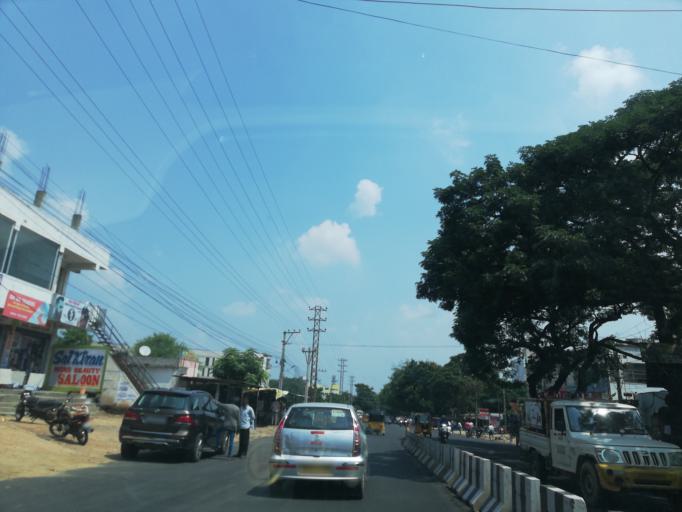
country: IN
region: Telangana
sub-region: Medak
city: Serilingampalle
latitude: 17.4800
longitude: 78.3200
